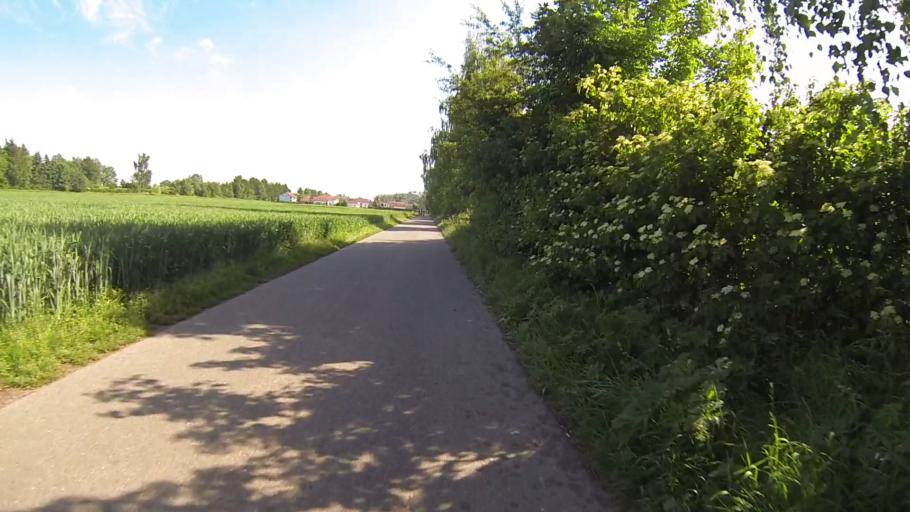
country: DE
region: Baden-Wuerttemberg
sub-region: Tuebingen Region
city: Laupheim
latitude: 48.1951
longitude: 9.8291
